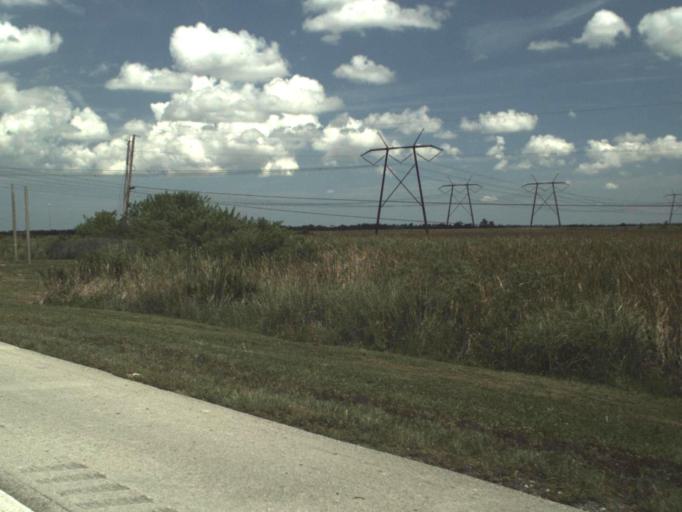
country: US
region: Florida
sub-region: Broward County
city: Weston
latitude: 26.1458
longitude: -80.4516
